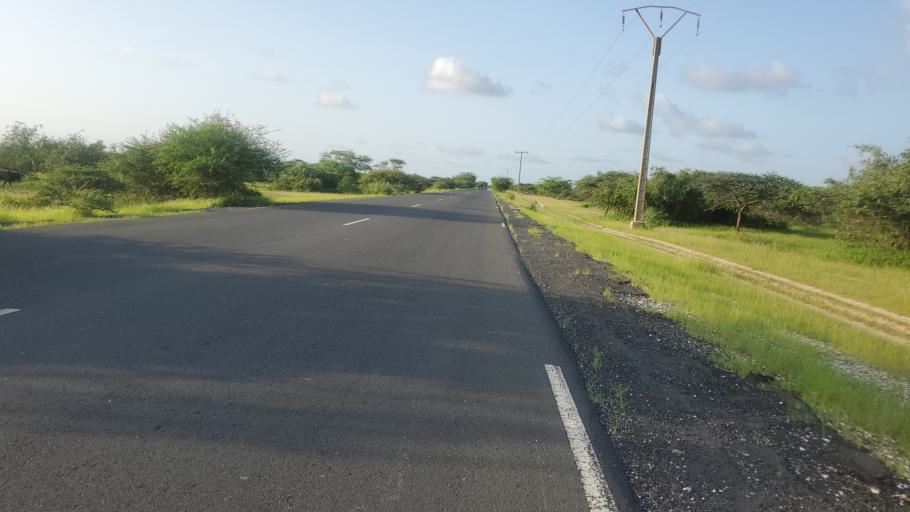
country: SN
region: Saint-Louis
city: Saint-Louis
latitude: 16.1768
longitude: -16.4096
